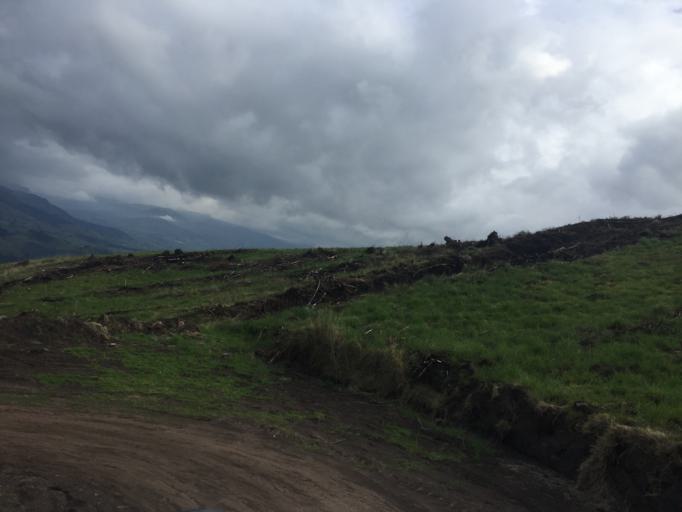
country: EC
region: Imbabura
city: Ibarra
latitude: 0.2265
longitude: -78.1217
